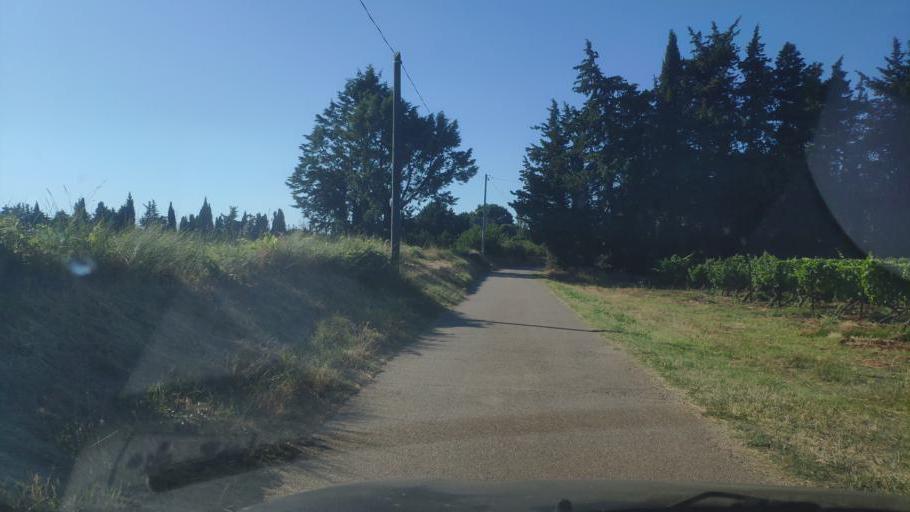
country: FR
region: Provence-Alpes-Cote d'Azur
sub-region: Departement du Vaucluse
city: Aubignan
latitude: 44.0797
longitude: 5.0456
